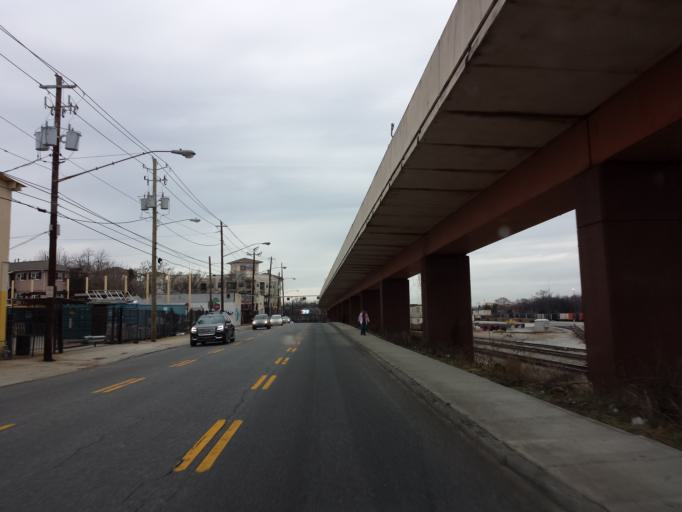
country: US
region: Georgia
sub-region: Fulton County
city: Atlanta
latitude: 33.7520
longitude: -84.3695
